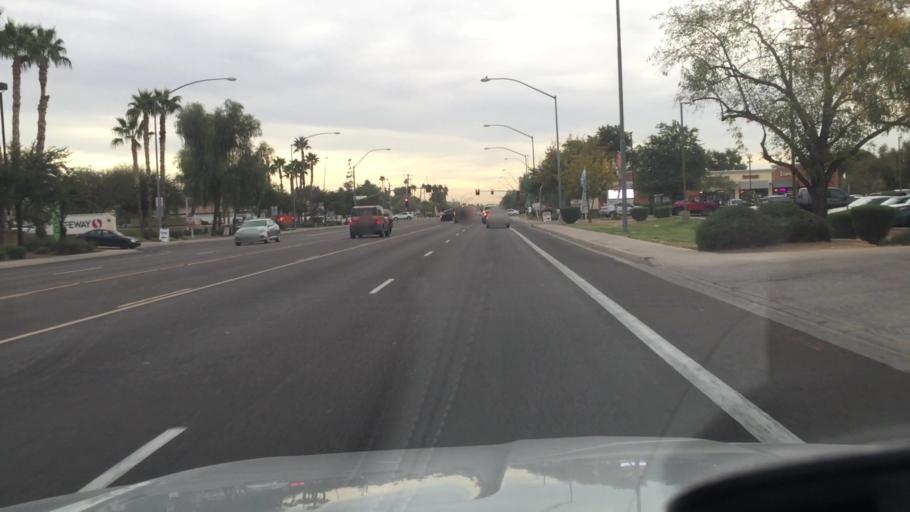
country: US
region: Arizona
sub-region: Maricopa County
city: Gilbert
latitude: 33.3955
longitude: -111.7539
